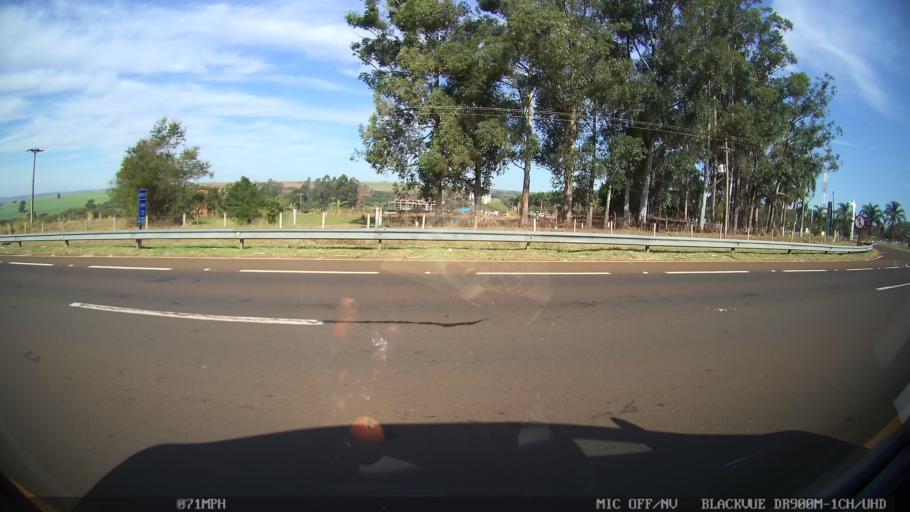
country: BR
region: Sao Paulo
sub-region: Americo Brasiliense
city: Americo Brasiliense
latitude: -21.7728
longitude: -48.0969
